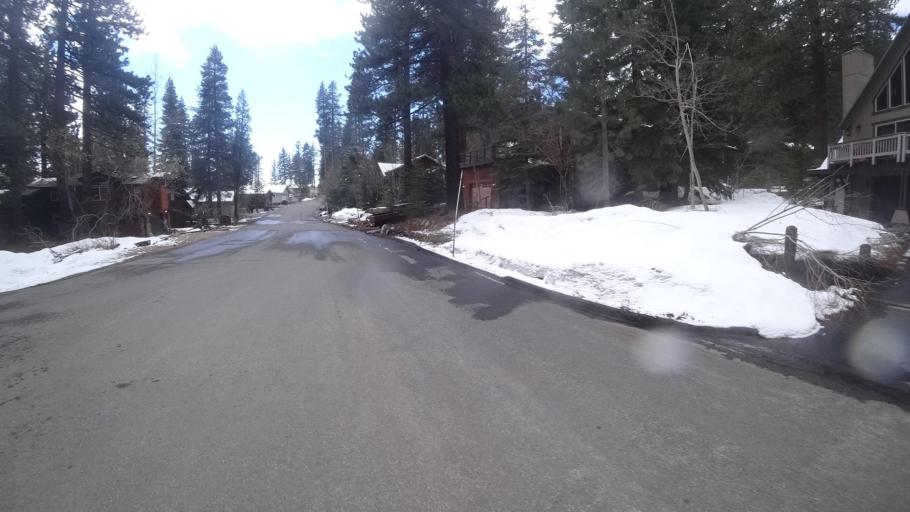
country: US
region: Nevada
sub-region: Washoe County
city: Incline Village
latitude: 39.2680
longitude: -119.9547
